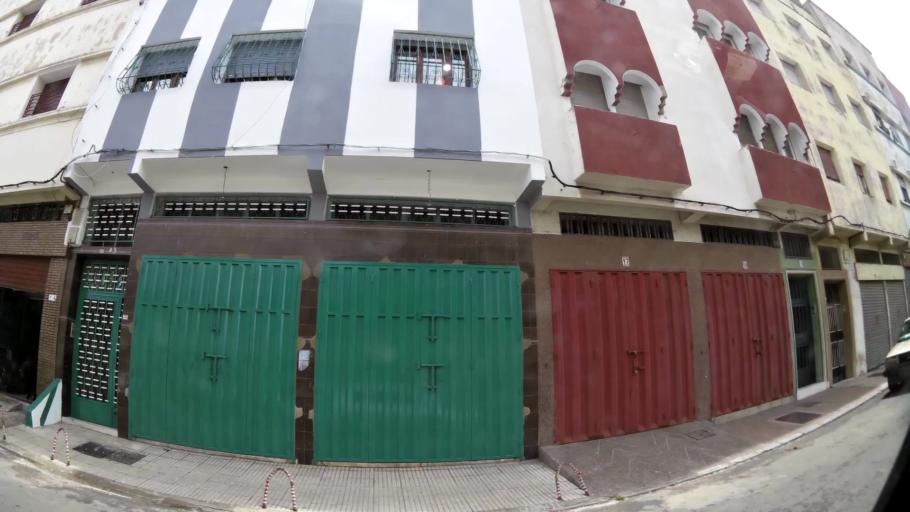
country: MA
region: Grand Casablanca
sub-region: Mediouna
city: Tit Mellil
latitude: 33.6030
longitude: -7.5164
